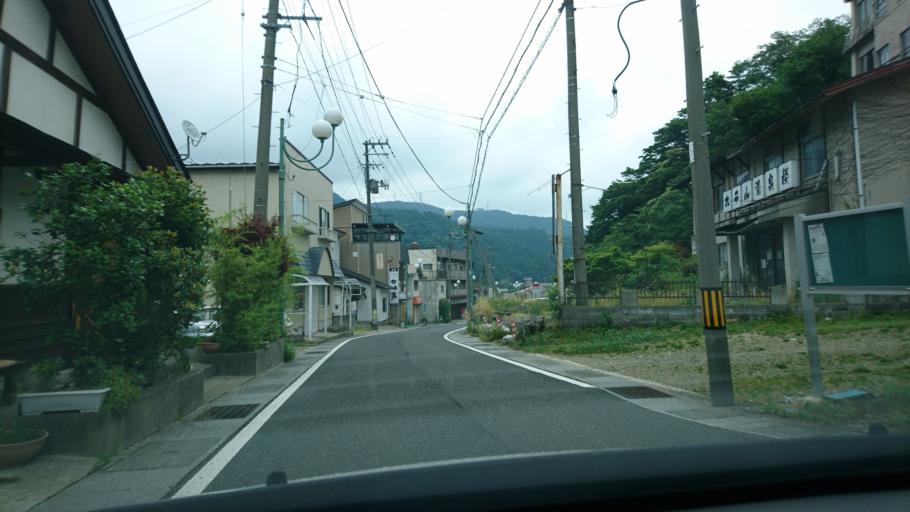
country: JP
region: Miyagi
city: Furukawa
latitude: 38.7471
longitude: 140.7200
